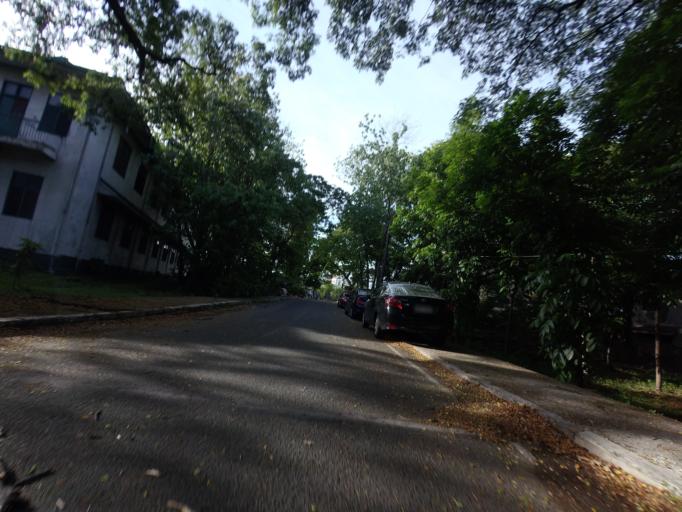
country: PH
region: Metro Manila
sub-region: Mandaluyong
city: Mandaluyong City
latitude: 14.5828
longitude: 121.0428
